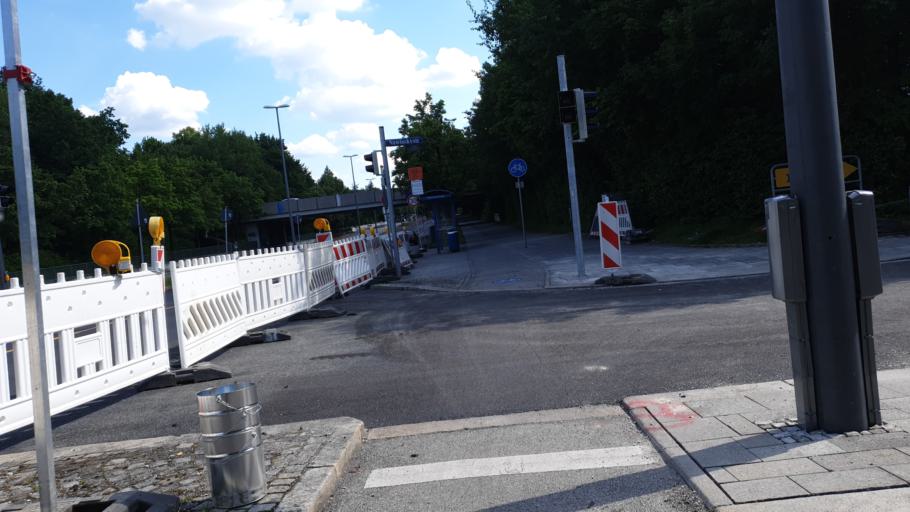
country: DE
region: Bavaria
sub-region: Upper Bavaria
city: Neubiberg
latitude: 48.1069
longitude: 11.6364
